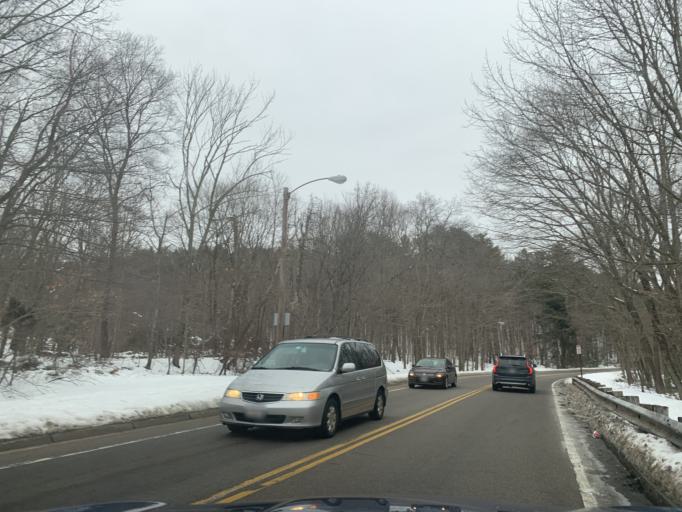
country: US
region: Massachusetts
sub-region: Norfolk County
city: Milton
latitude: 42.2089
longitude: -71.1023
